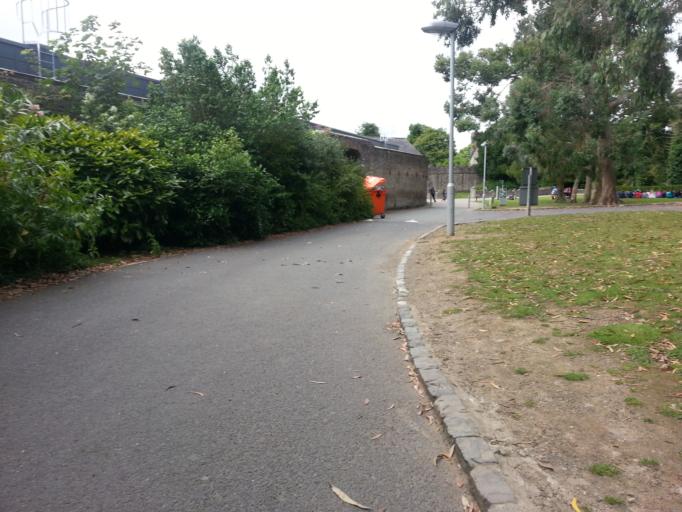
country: IE
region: Leinster
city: Malahide
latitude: 53.4455
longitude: -6.1622
